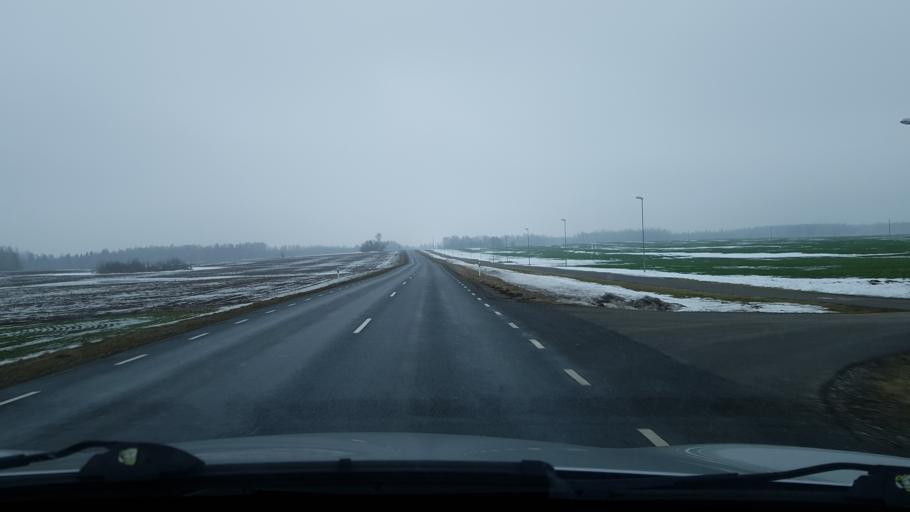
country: EE
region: Valgamaa
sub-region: Torva linn
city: Torva
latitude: 58.2184
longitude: 25.9051
